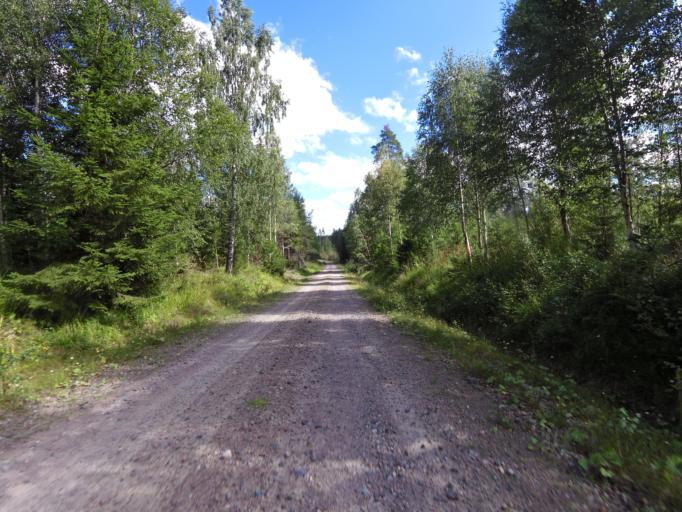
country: SE
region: Gaevleborg
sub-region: Hofors Kommun
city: Hofors
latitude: 60.5202
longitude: 16.2601
